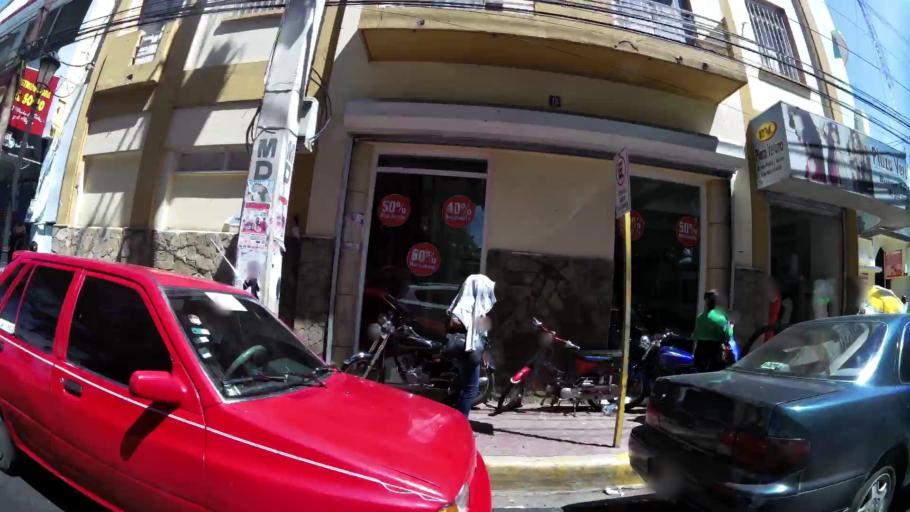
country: DO
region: Santiago
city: Santiago de los Caballeros
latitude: 19.4507
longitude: -70.7061
